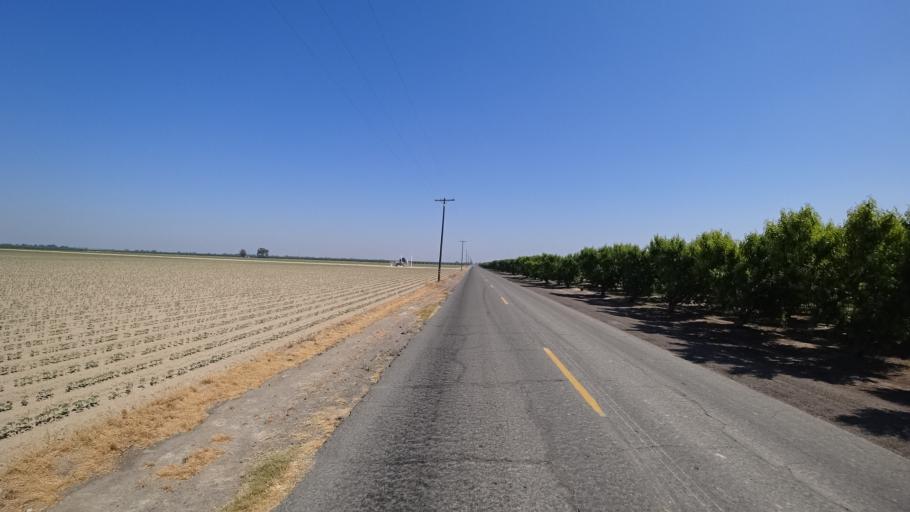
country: US
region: California
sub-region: Fresno County
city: Kingsburg
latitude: 36.4254
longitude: -119.5287
